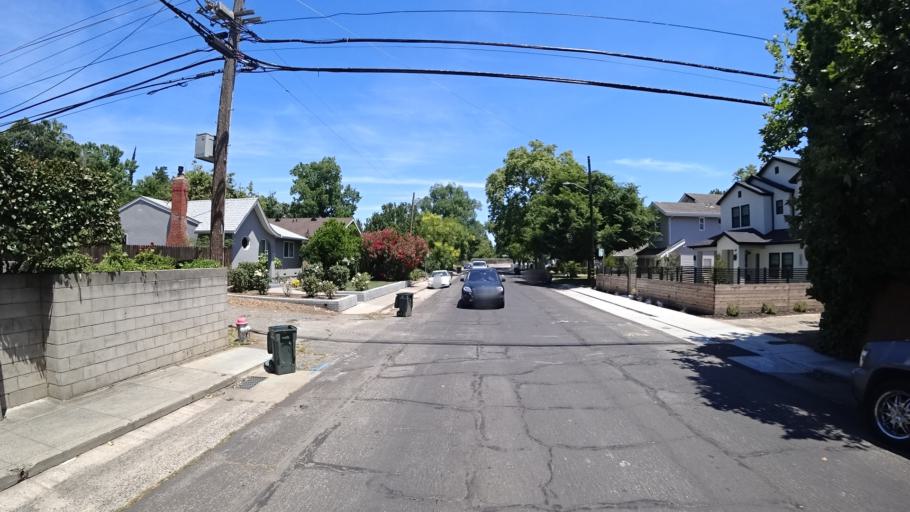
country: US
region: California
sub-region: Sacramento County
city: Sacramento
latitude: 38.5565
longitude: -121.4493
